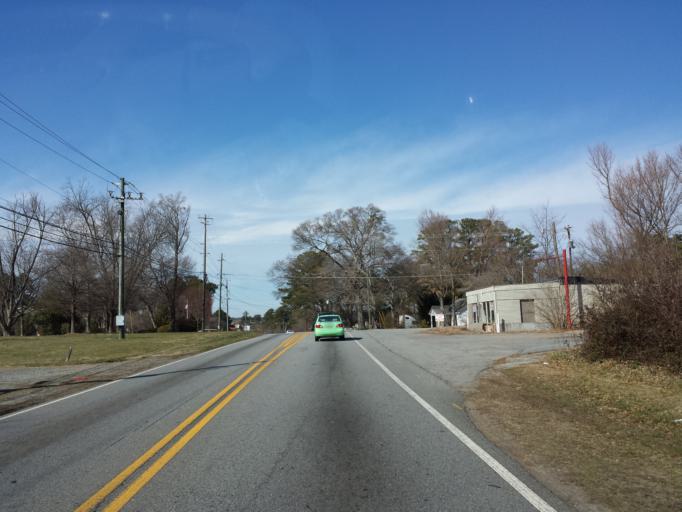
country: US
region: Georgia
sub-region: Cobb County
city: Kennesaw
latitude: 33.9979
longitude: -84.5993
